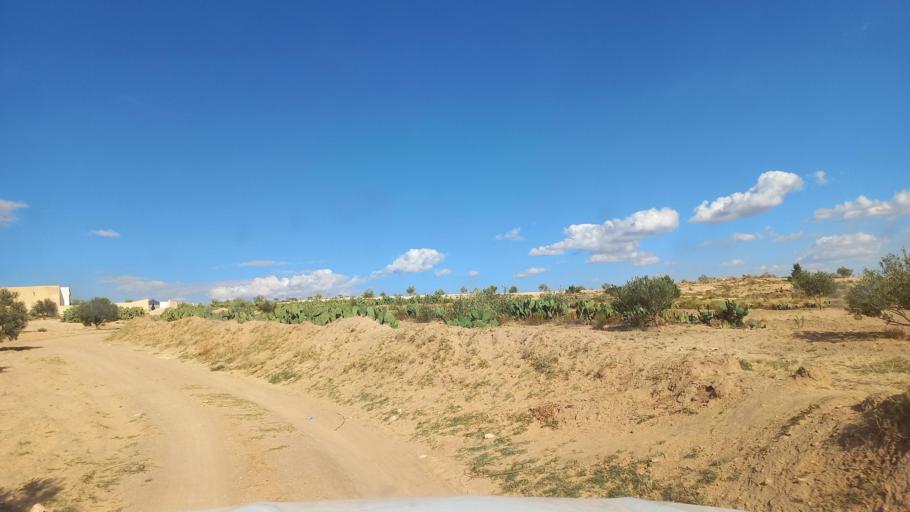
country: TN
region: Al Qasrayn
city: Sbiba
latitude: 35.4010
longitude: 9.0129
